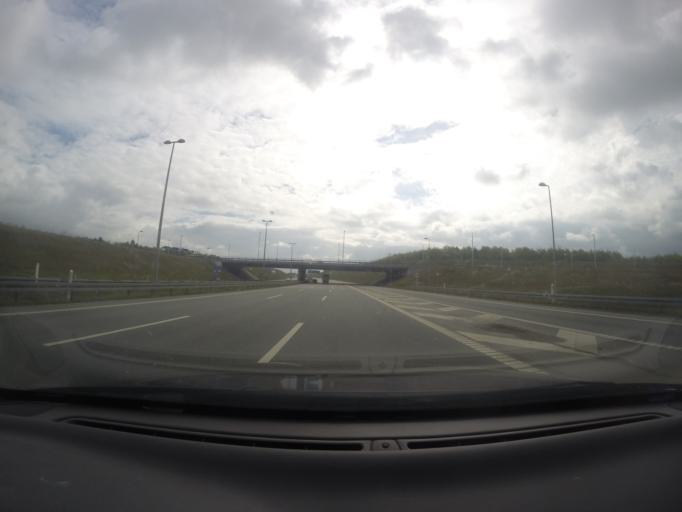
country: DK
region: Capital Region
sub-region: Glostrup Kommune
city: Glostrup
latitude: 55.6925
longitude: 12.4052
